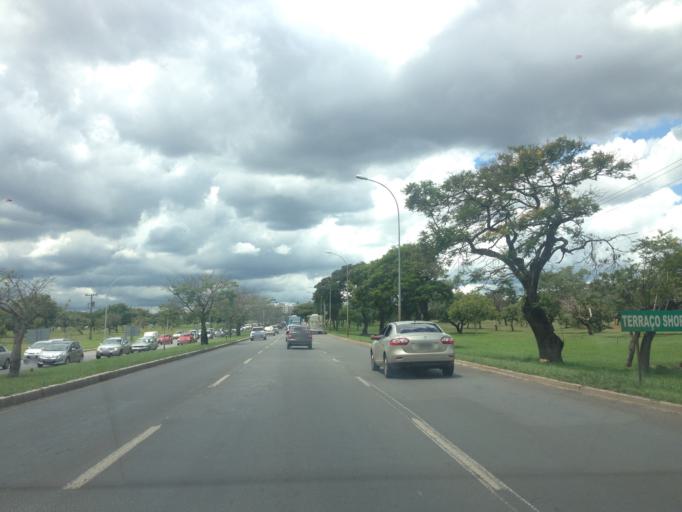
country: BR
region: Federal District
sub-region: Brasilia
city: Brasilia
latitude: -15.8160
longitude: -47.9373
